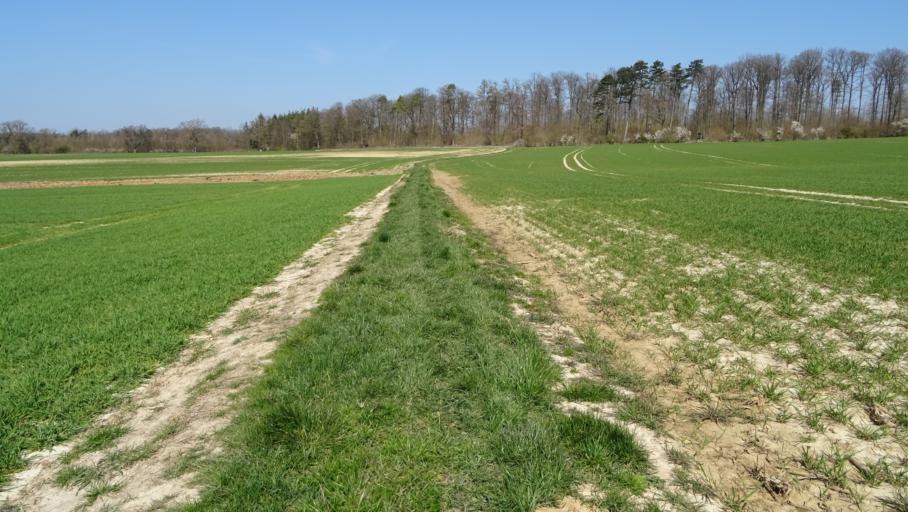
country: DE
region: Baden-Wuerttemberg
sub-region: Karlsruhe Region
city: Seckach
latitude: 49.4078
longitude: 9.3129
